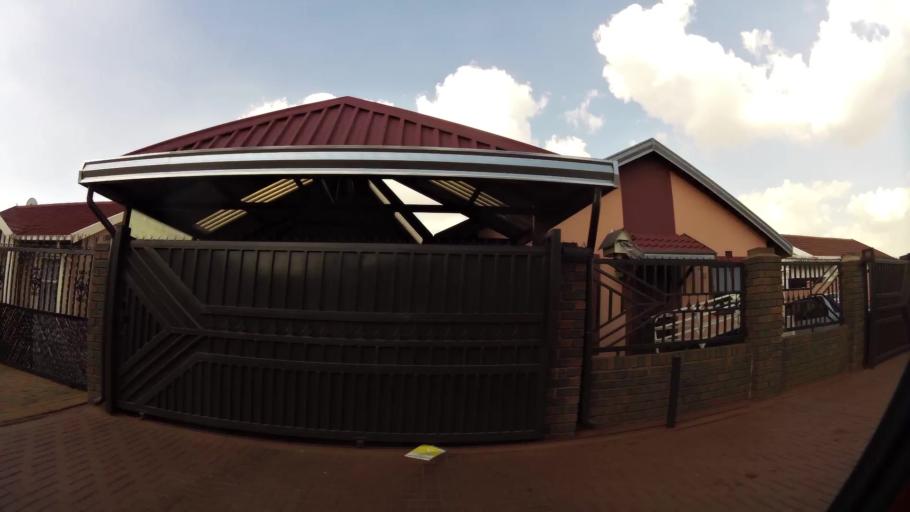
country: ZA
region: Gauteng
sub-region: City of Johannesburg Metropolitan Municipality
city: Roodepoort
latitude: -26.2120
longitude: 27.8662
